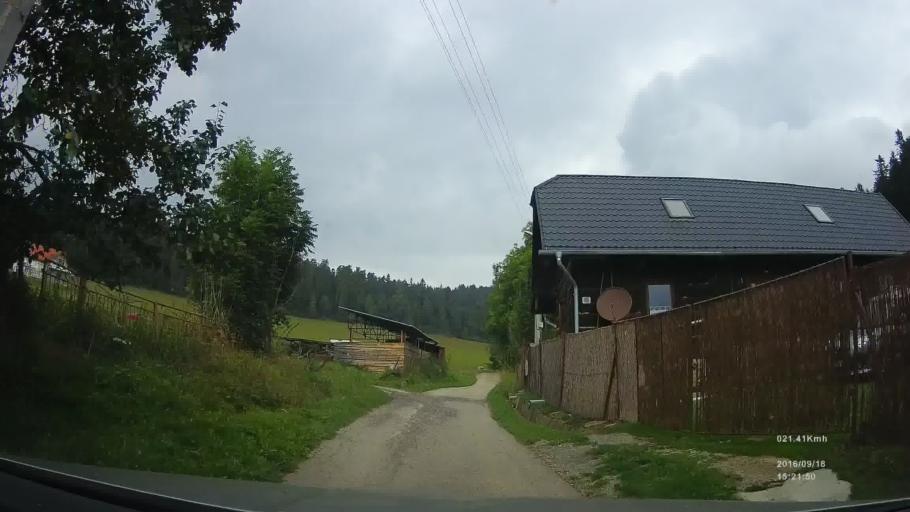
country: SK
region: Presovsky
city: Lubica
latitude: 49.0421
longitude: 20.4872
